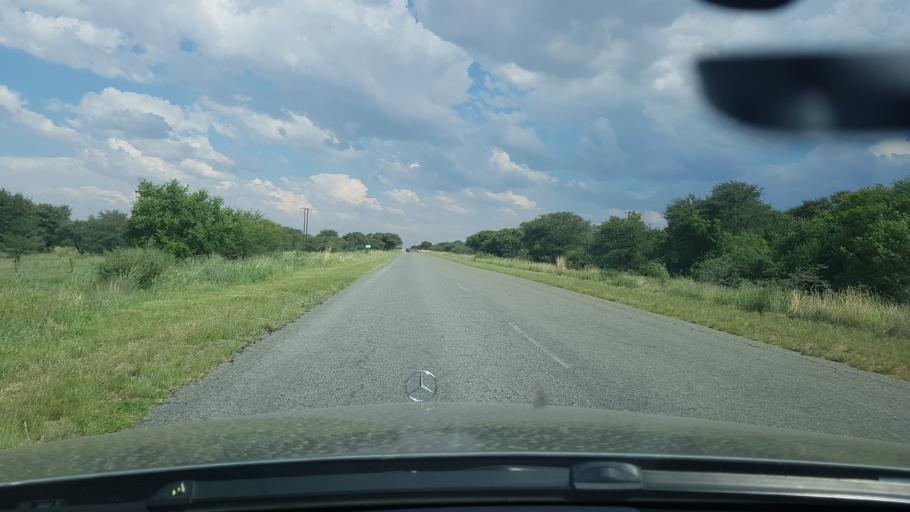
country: ZA
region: North-West
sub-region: Dr Ruth Segomotsi Mompati District Municipality
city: Bloemhof
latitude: -27.7938
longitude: 25.6161
